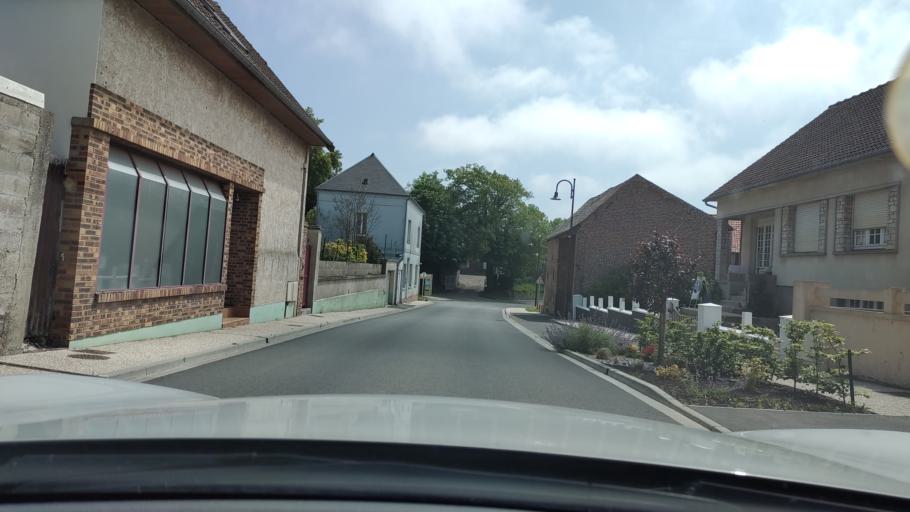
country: FR
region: Picardie
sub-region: Departement de la Somme
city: Ault
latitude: 50.0698
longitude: 1.4603
